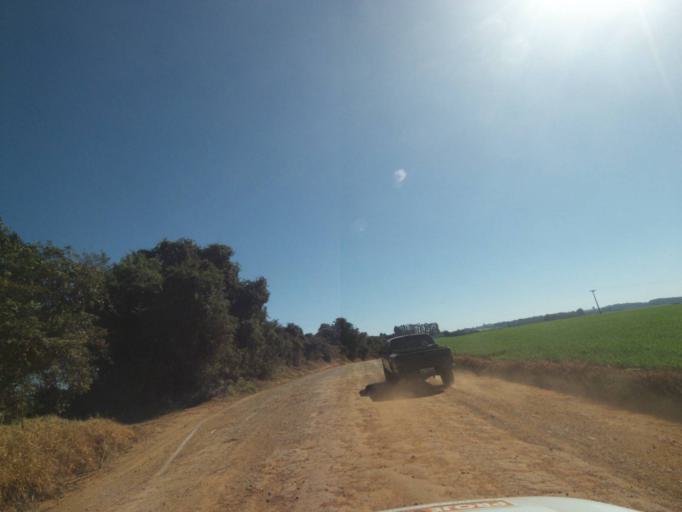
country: BR
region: Parana
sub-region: Reserva
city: Reserva
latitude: -24.6275
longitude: -50.6257
